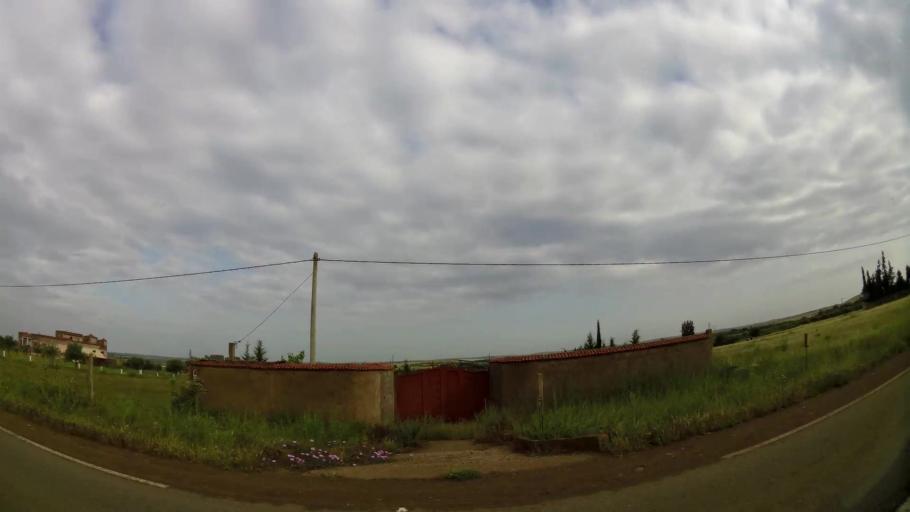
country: MA
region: Rabat-Sale-Zemmour-Zaer
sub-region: Khemisset
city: Khemisset
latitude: 33.7615
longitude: -6.1769
